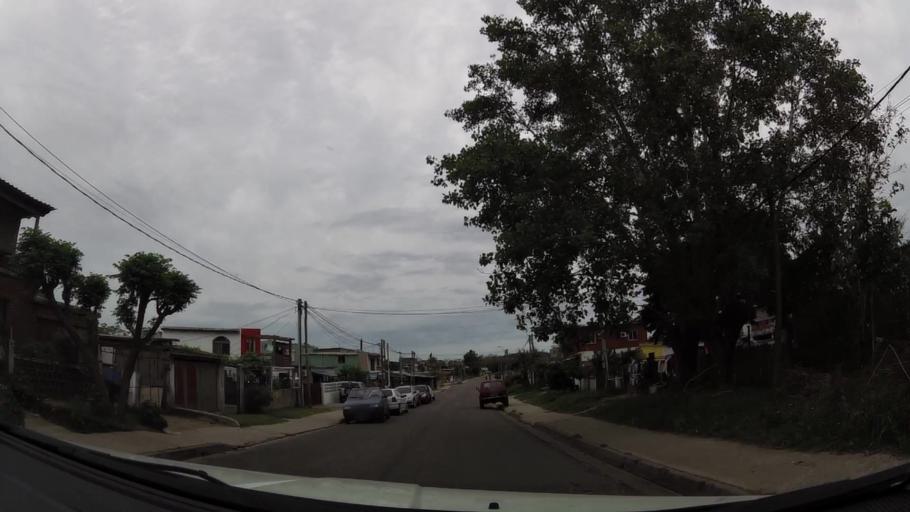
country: UY
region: Maldonado
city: Maldonado
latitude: -34.8954
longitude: -54.9361
